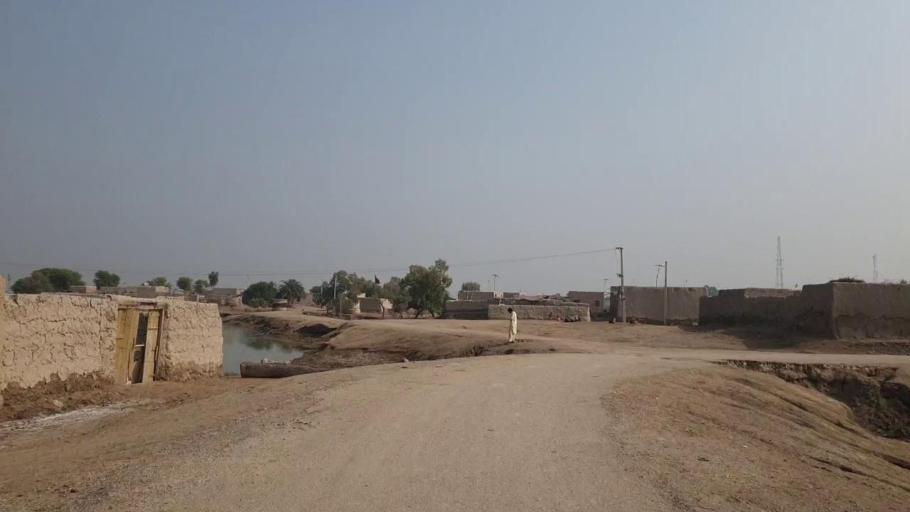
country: PK
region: Sindh
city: Bhan
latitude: 26.4474
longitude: 67.7149
